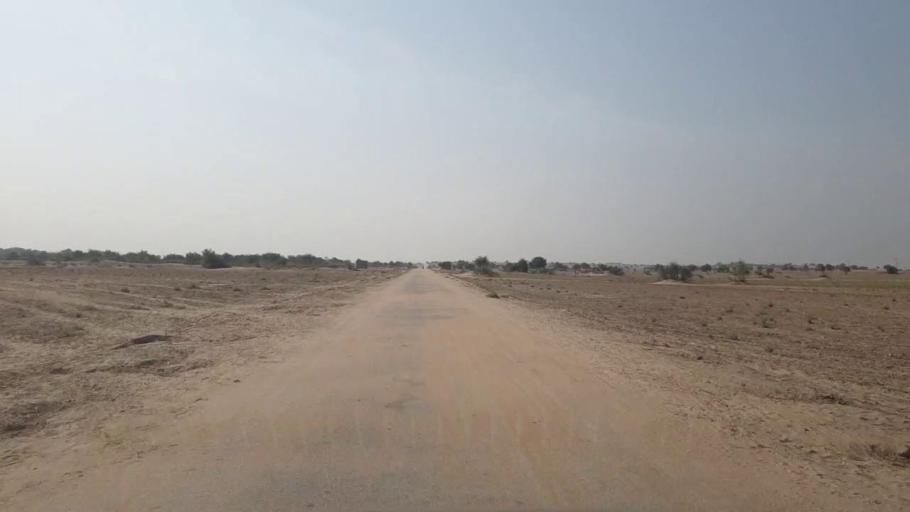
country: PK
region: Sindh
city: Umarkot
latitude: 25.3111
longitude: 69.7288
